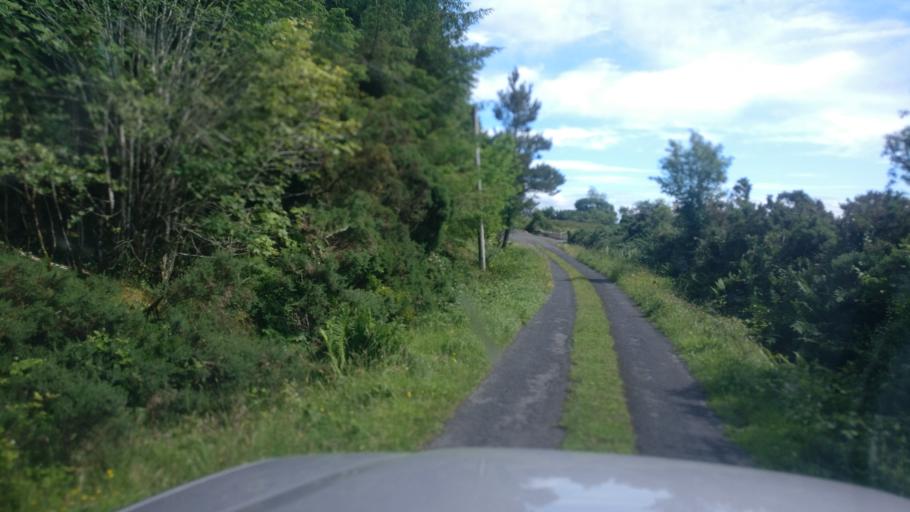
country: IE
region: Connaught
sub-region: County Galway
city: Gort
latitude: 53.0737
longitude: -8.7081
